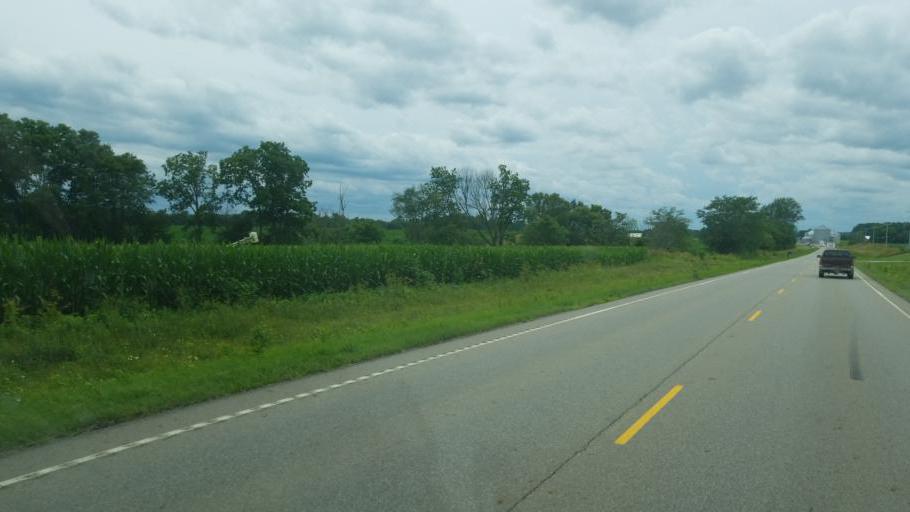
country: US
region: Ohio
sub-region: Licking County
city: Utica
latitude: 40.2315
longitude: -82.4885
